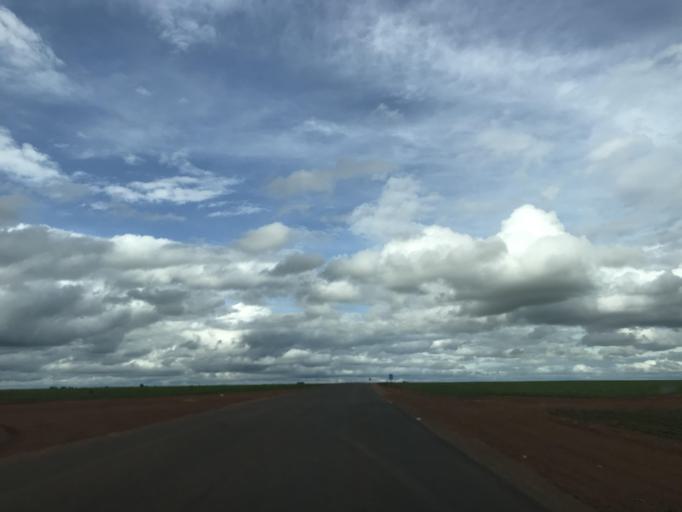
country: BR
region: Goias
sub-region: Vianopolis
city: Vianopolis
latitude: -16.9735
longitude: -48.6593
